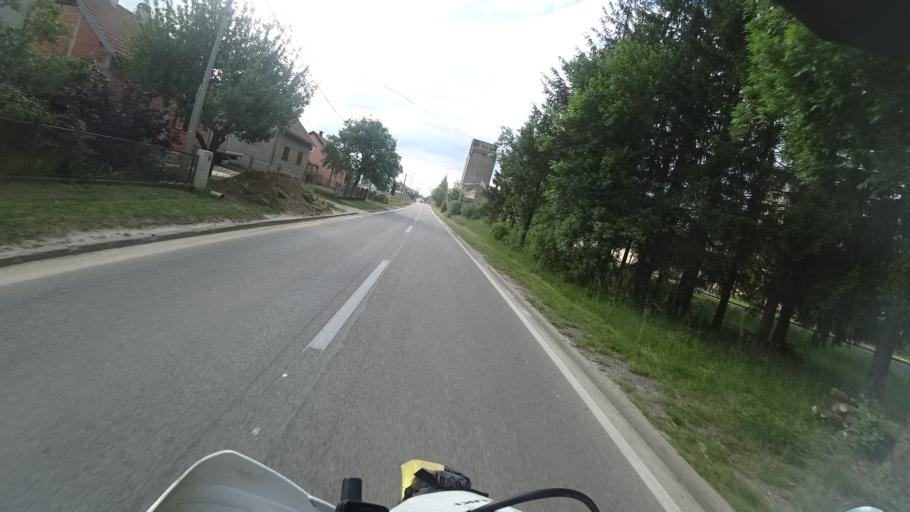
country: HR
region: Licko-Senjska
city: Gospic
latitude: 44.5328
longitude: 15.3987
